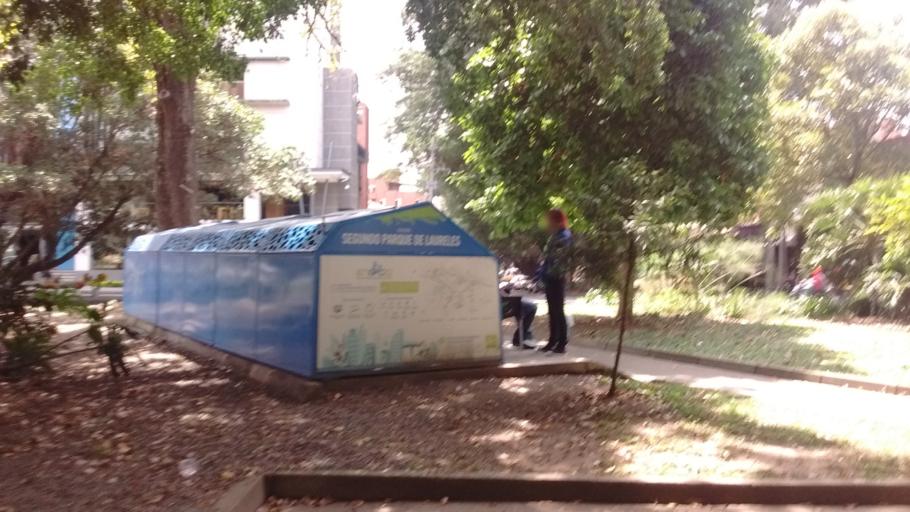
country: CO
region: Antioquia
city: Medellin
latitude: 6.2450
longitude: -75.5971
